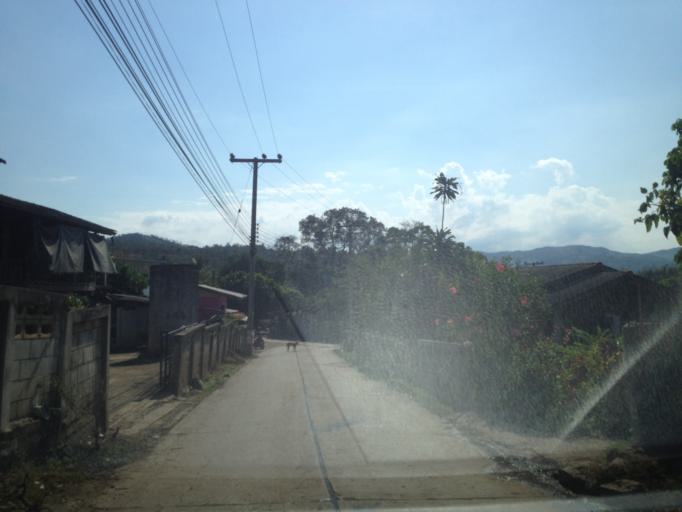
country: TH
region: Mae Hong Son
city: Ban Huai I Huak
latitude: 18.0950
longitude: 98.2055
